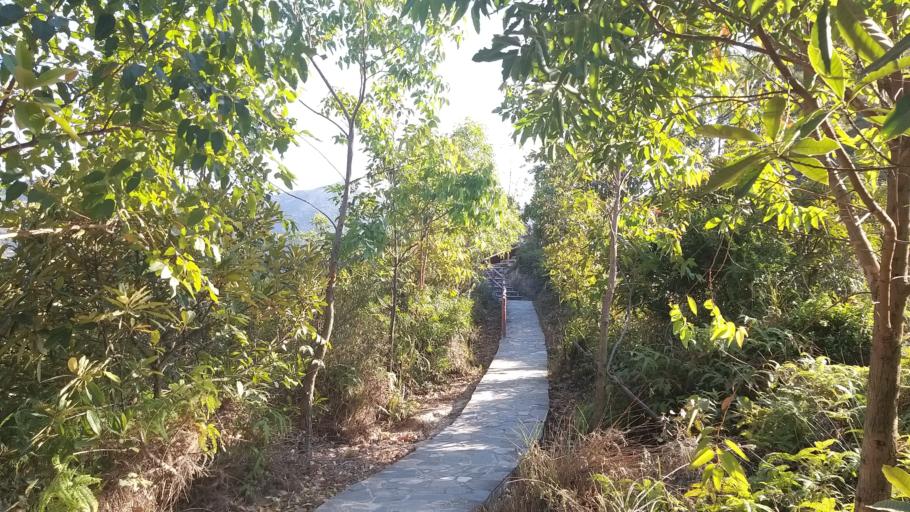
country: HK
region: Tuen Mun
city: Tuen Mun
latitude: 22.4010
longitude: 113.9877
